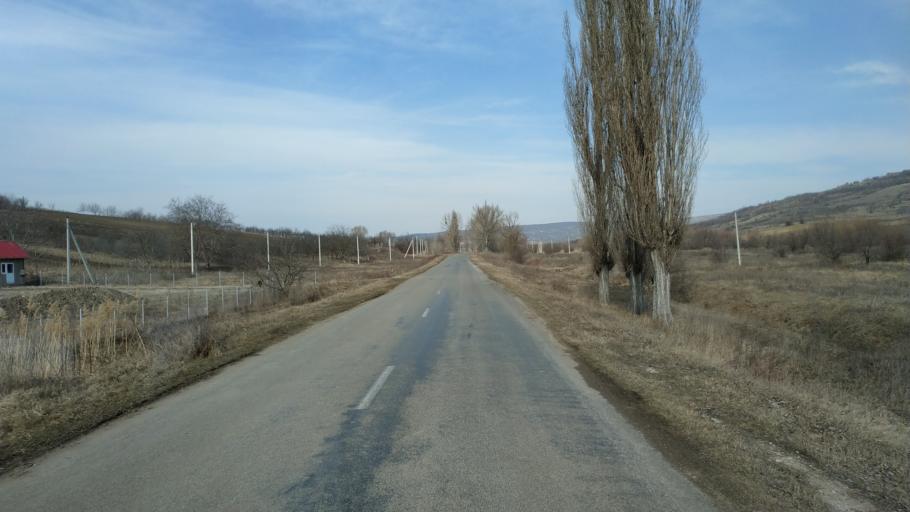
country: MD
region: Nisporeni
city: Nisporeni
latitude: 47.1560
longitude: 28.1070
